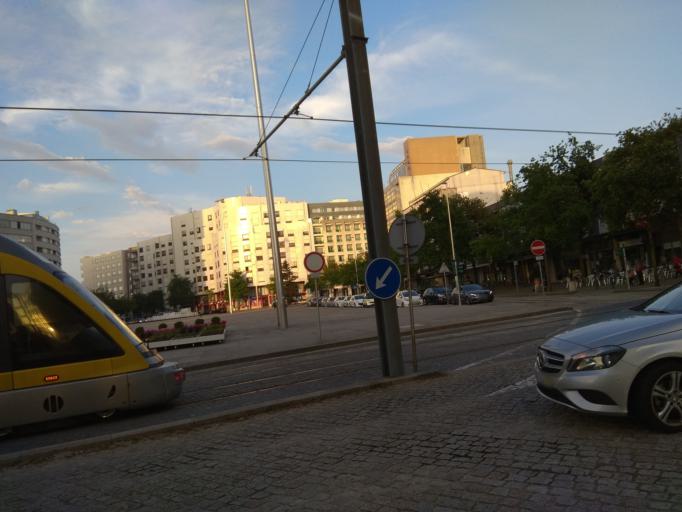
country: PT
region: Porto
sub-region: Maia
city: Maia
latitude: 41.2328
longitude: -8.6232
